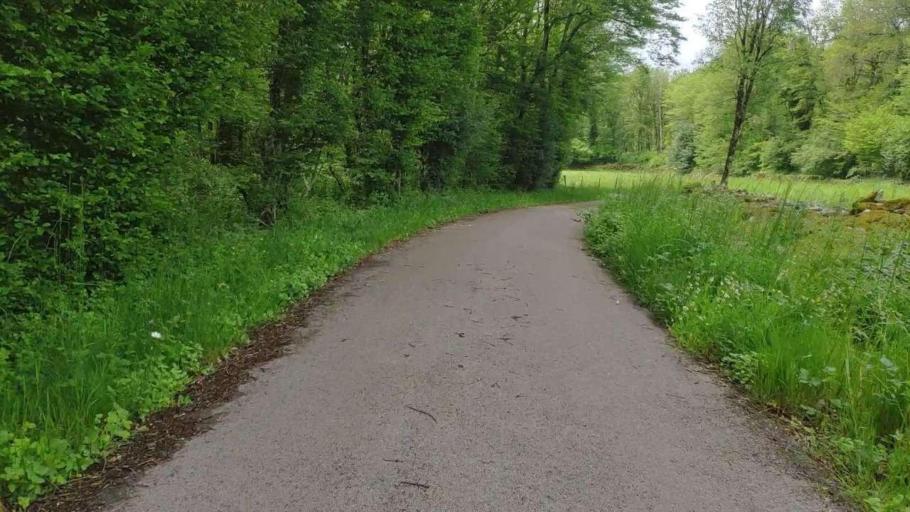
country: FR
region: Franche-Comte
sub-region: Departement du Jura
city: Perrigny
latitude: 46.7442
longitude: 5.6423
